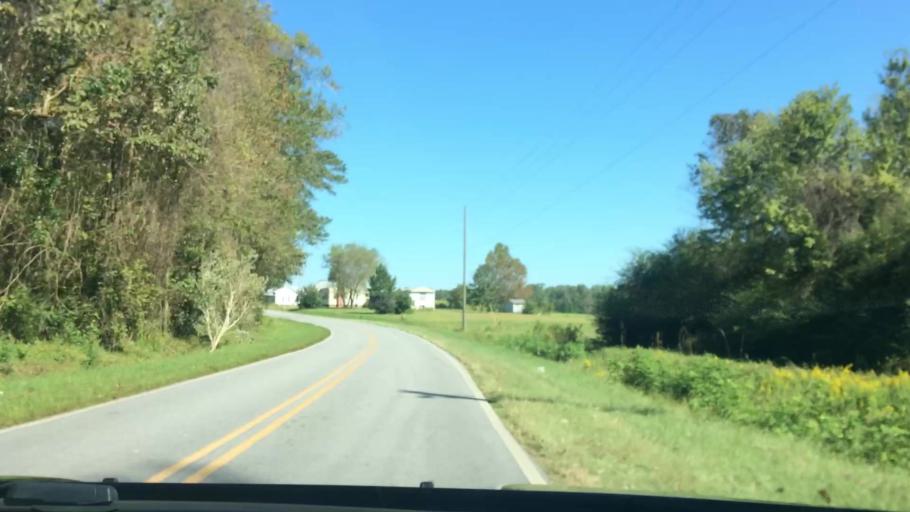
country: US
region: North Carolina
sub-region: Pitt County
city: Winterville
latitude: 35.5143
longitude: -77.4315
